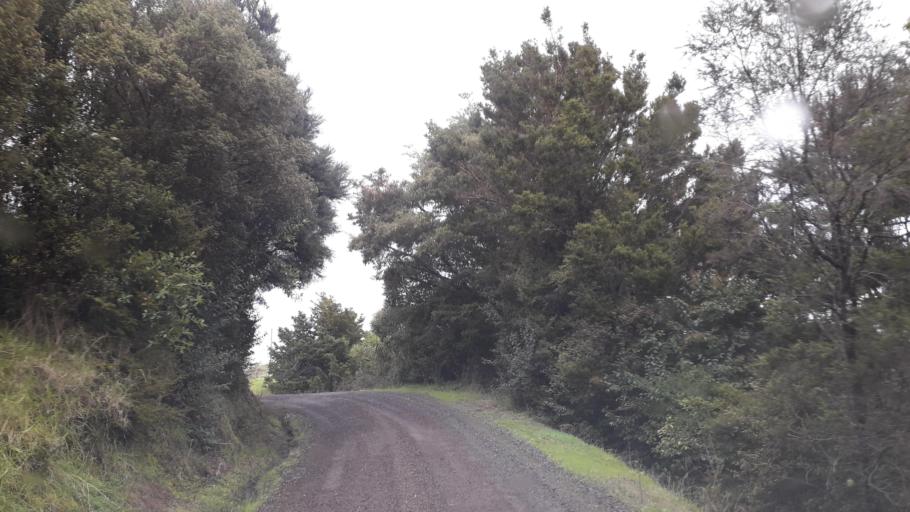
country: NZ
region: Northland
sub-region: Far North District
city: Waimate North
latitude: -35.3108
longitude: 173.5638
